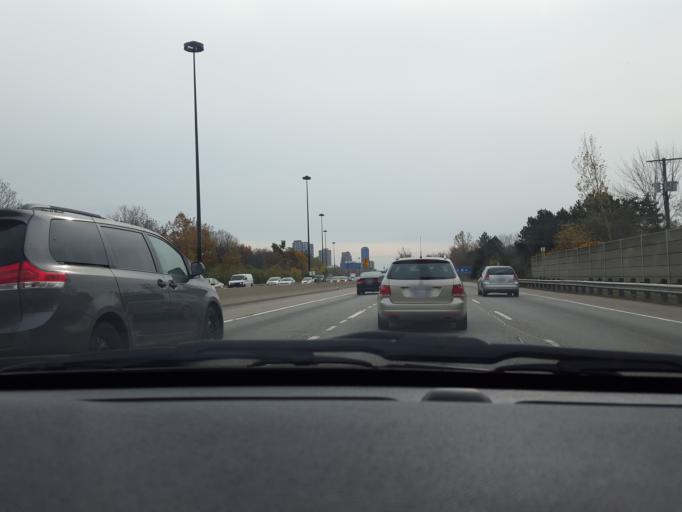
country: CA
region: Ontario
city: Willowdale
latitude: 43.7484
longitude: -79.3335
